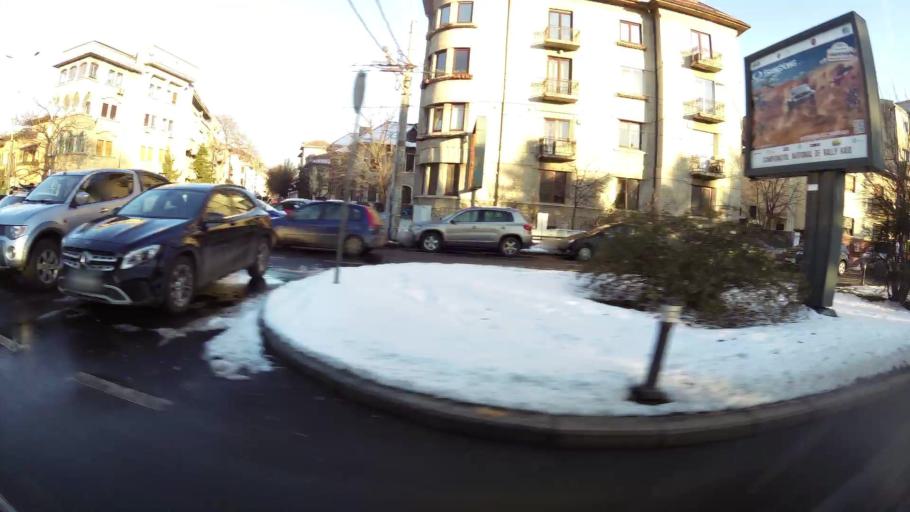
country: RO
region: Bucuresti
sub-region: Municipiul Bucuresti
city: Bucuresti
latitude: 44.4355
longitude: 26.0668
